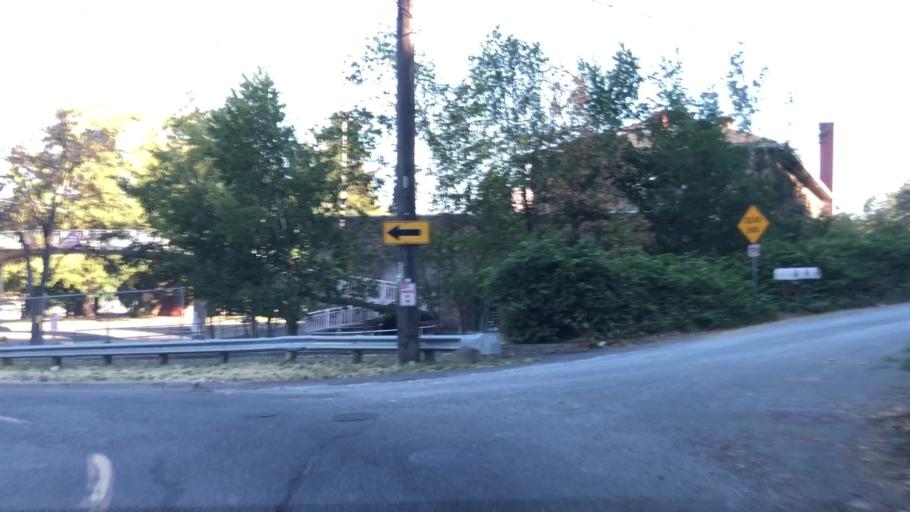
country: US
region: Washington
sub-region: King County
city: White Center
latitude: 47.5628
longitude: -122.3629
